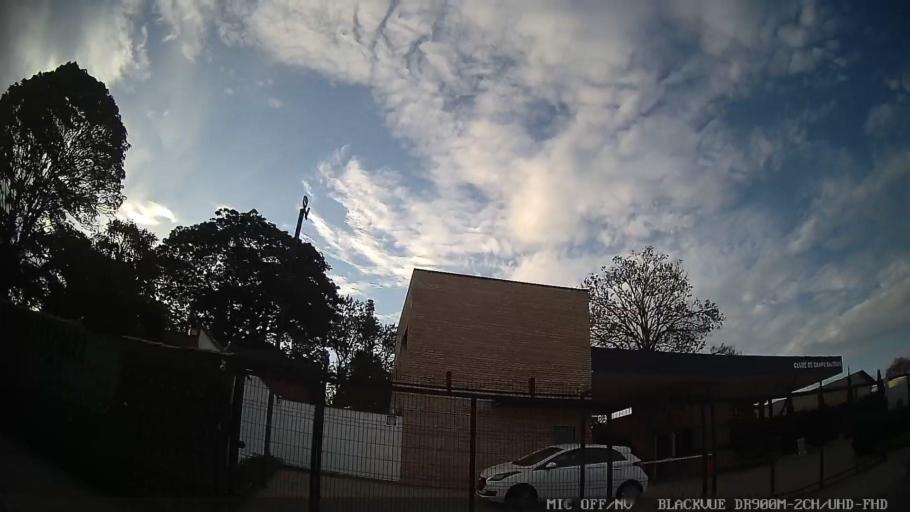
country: BR
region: Sao Paulo
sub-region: Salto
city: Salto
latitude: -23.1965
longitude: -47.2767
